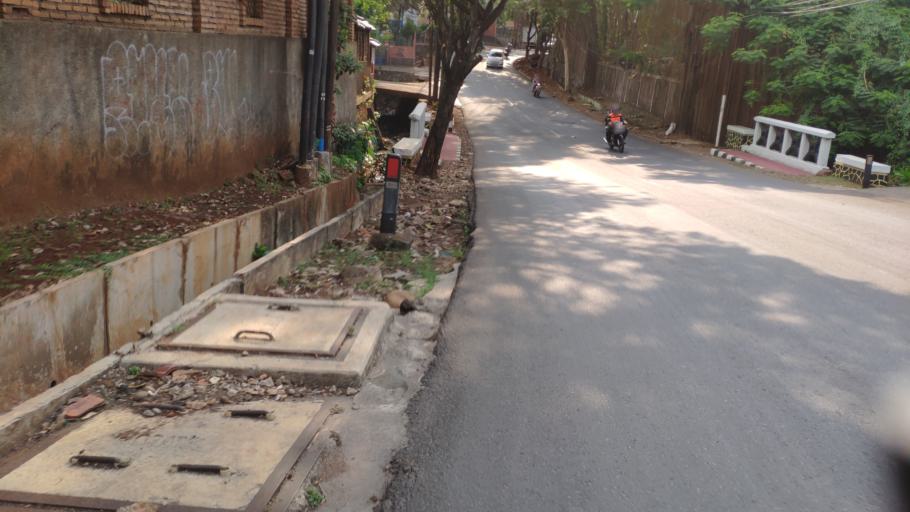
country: ID
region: West Java
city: Pamulang
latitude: -6.3108
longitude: 106.8119
